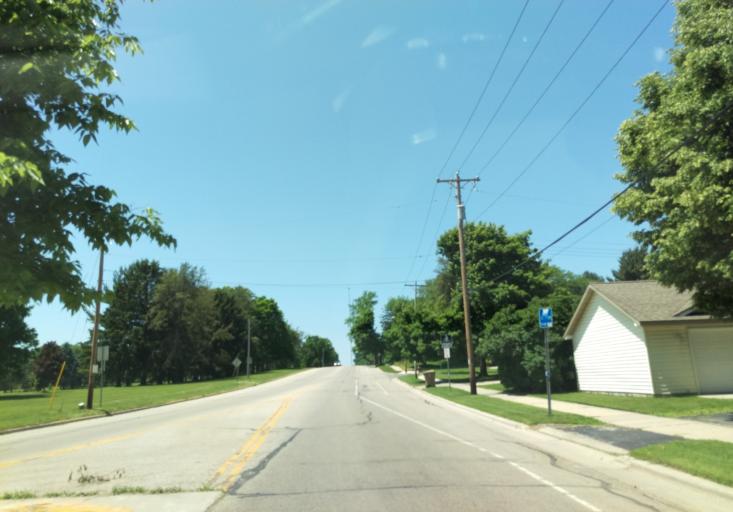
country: US
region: Wisconsin
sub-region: Dane County
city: Shorewood Hills
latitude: 43.0499
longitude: -89.4551
